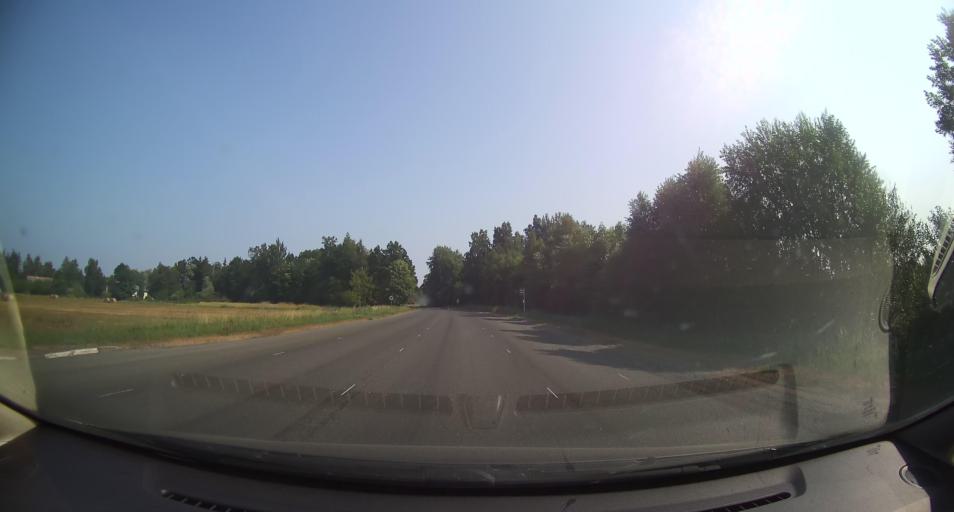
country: EE
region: Paernumaa
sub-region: Audru vald
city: Audru
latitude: 58.4452
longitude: 24.3086
